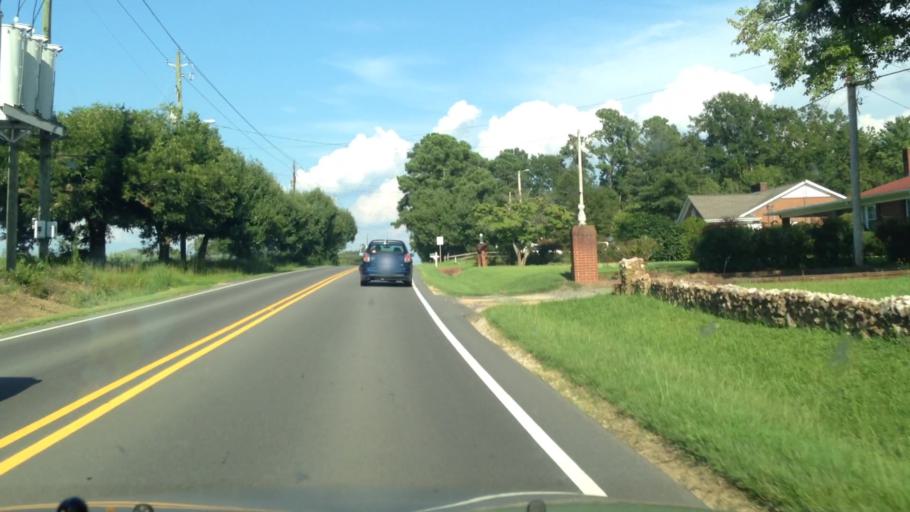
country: US
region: North Carolina
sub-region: Harnett County
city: Coats
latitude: 35.4125
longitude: -78.6772
